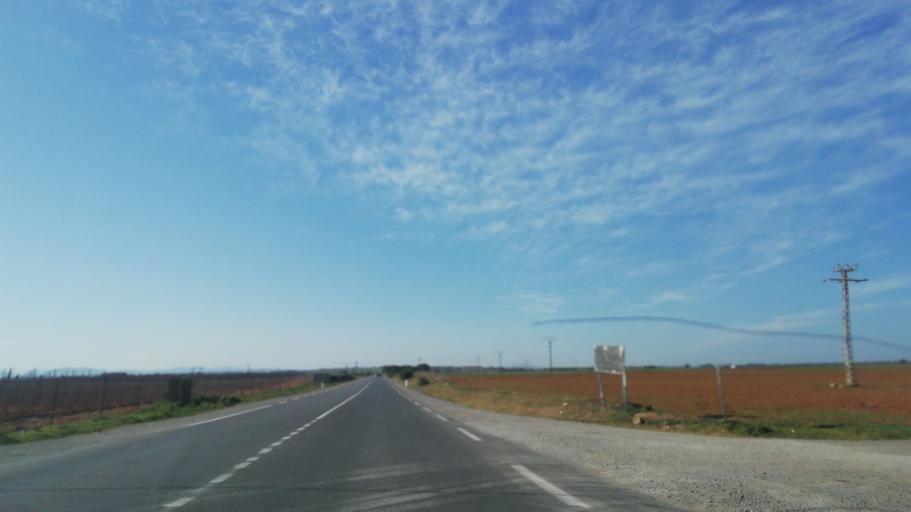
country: DZ
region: Tlemcen
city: Ouled Mimoun
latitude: 35.0366
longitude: -0.8563
